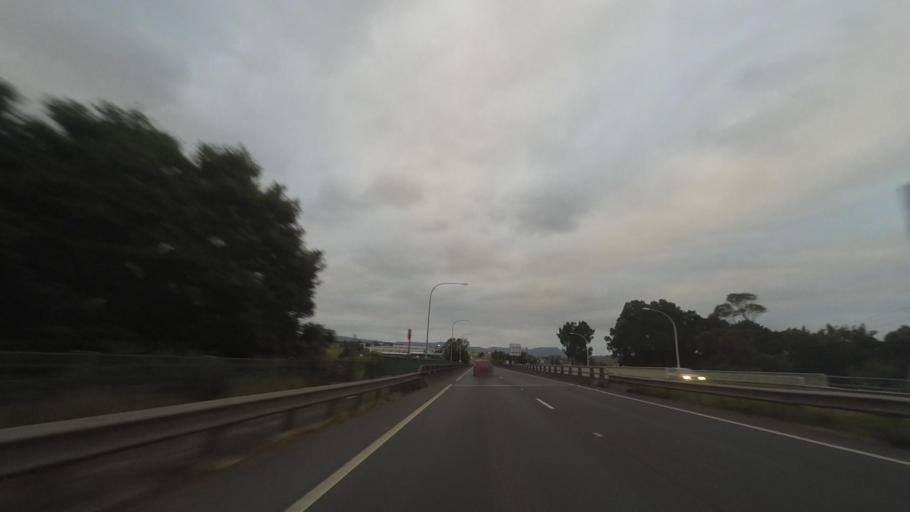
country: AU
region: New South Wales
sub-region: Shellharbour
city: Albion Park Rail
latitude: -34.5474
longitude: 150.7850
